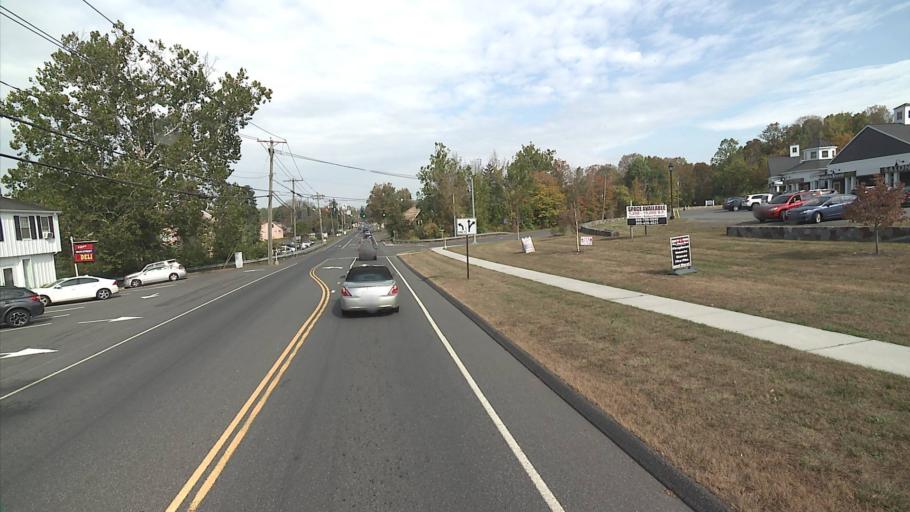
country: US
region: Connecticut
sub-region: Litchfield County
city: Woodbury Center
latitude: 41.5234
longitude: -73.2024
